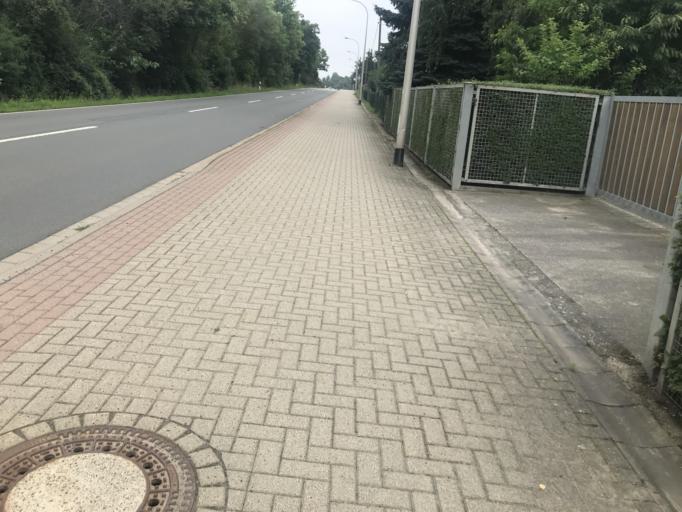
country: DE
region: Saxony-Anhalt
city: Quedlinburg
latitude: 51.7939
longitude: 11.1193
